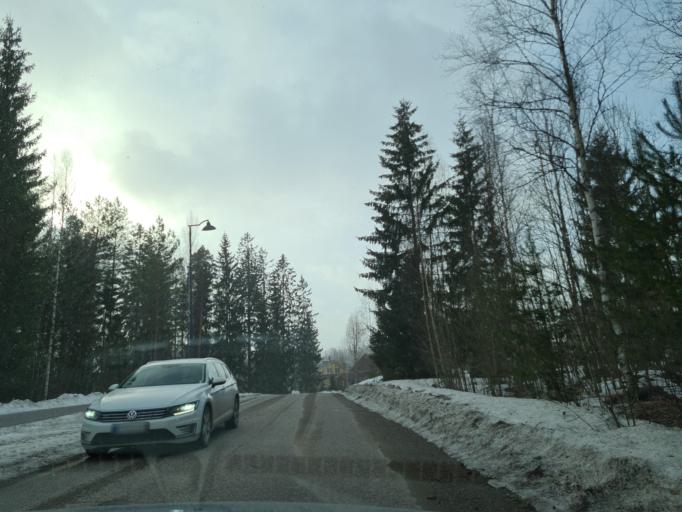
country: FI
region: Uusimaa
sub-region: Helsinki
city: Maentsaelae
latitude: 60.6539
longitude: 25.3106
